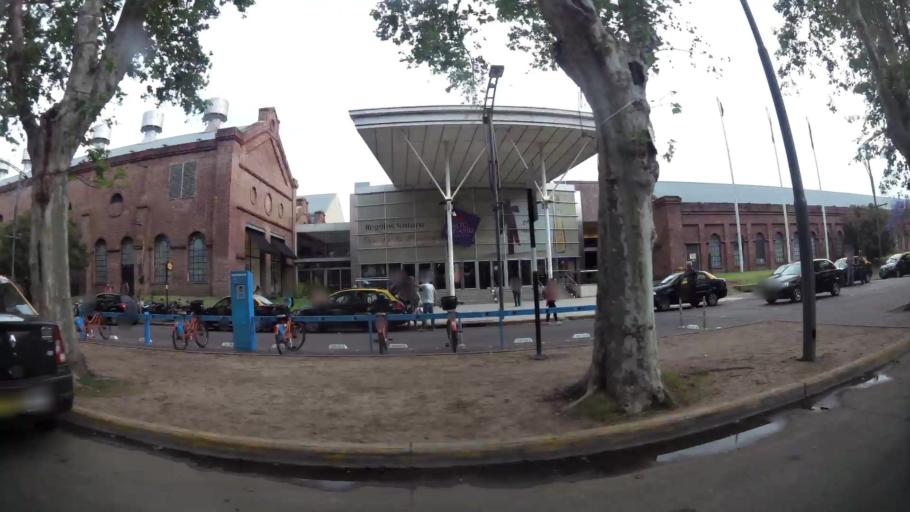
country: AR
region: Santa Fe
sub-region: Departamento de Rosario
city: Rosario
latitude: -32.9265
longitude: -60.6690
